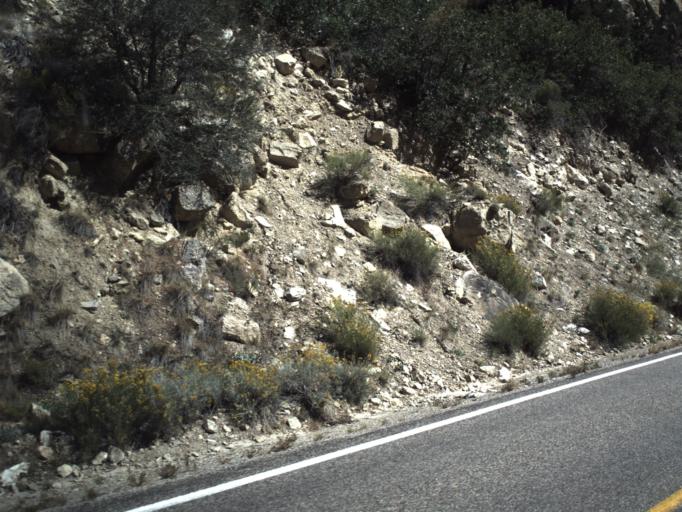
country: US
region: Utah
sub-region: Iron County
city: Cedar City
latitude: 37.6427
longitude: -112.9572
